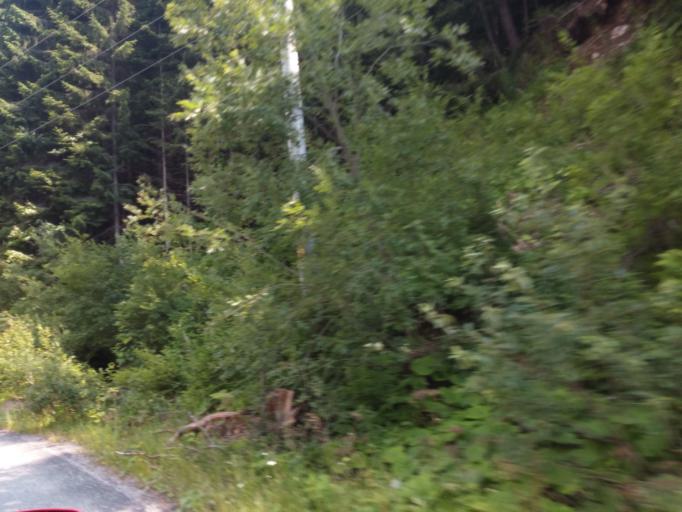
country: RO
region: Valcea
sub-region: Comuna Voineasa
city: Voineasa
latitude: 45.4298
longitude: 23.8347
